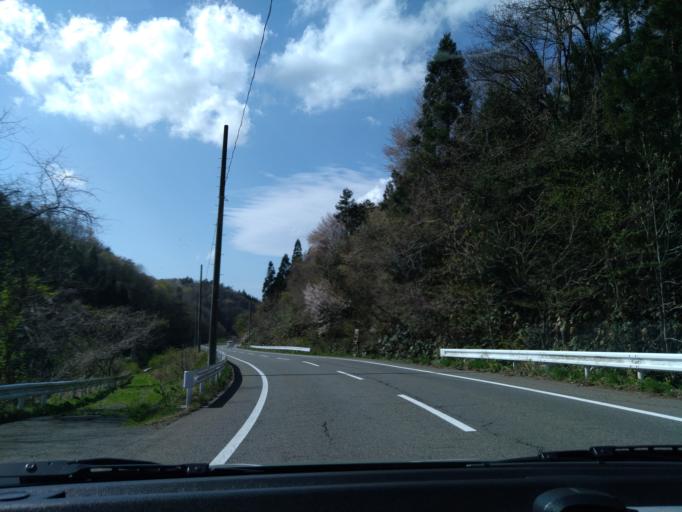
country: JP
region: Akita
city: Akita
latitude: 39.6985
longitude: 140.2209
